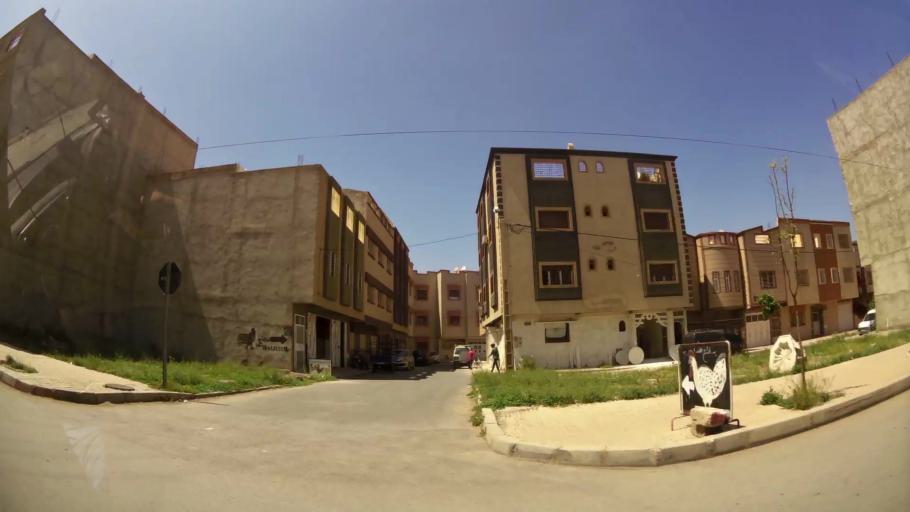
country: MA
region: Oriental
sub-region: Oujda-Angad
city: Oujda
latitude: 34.6926
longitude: -1.8868
